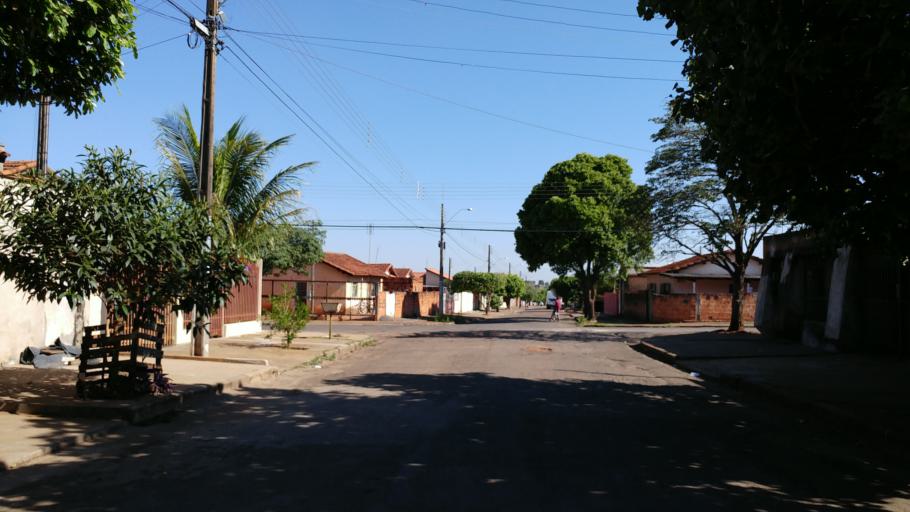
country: BR
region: Sao Paulo
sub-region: Paraguacu Paulista
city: Paraguacu Paulista
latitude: -22.4327
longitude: -50.5820
